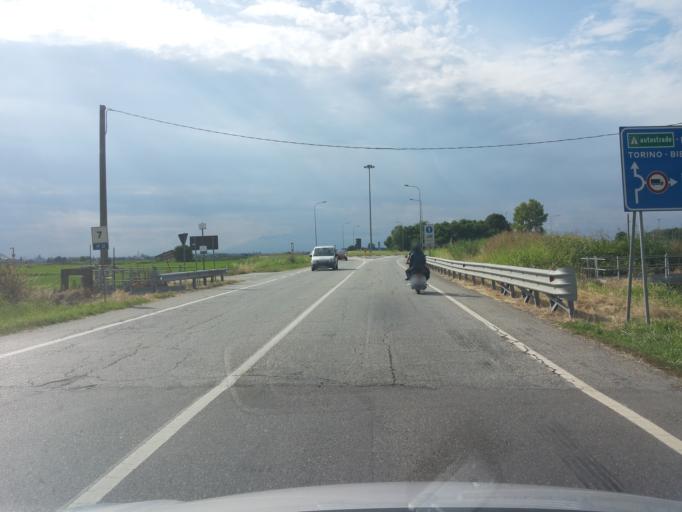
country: IT
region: Piedmont
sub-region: Provincia di Vercelli
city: Prarolo
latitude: 45.2889
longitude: 8.4552
